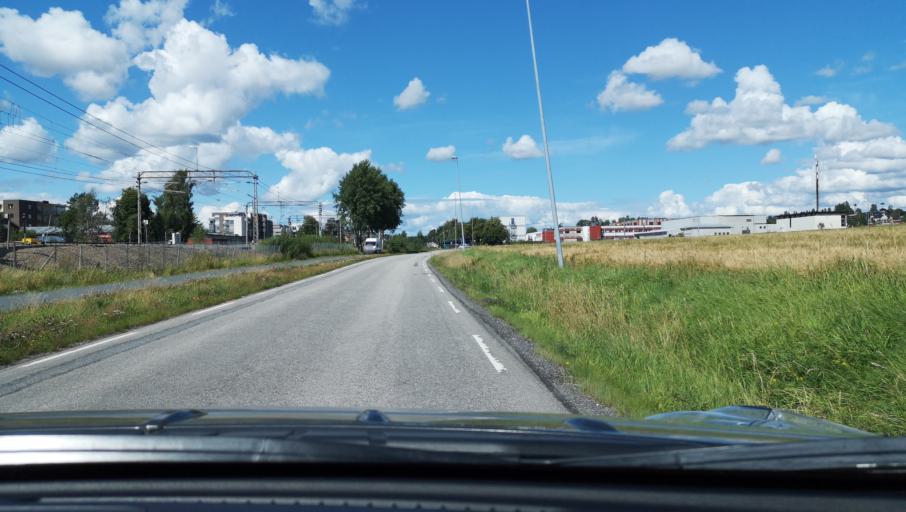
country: NO
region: Akershus
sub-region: As
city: As
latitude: 59.6596
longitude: 10.7970
